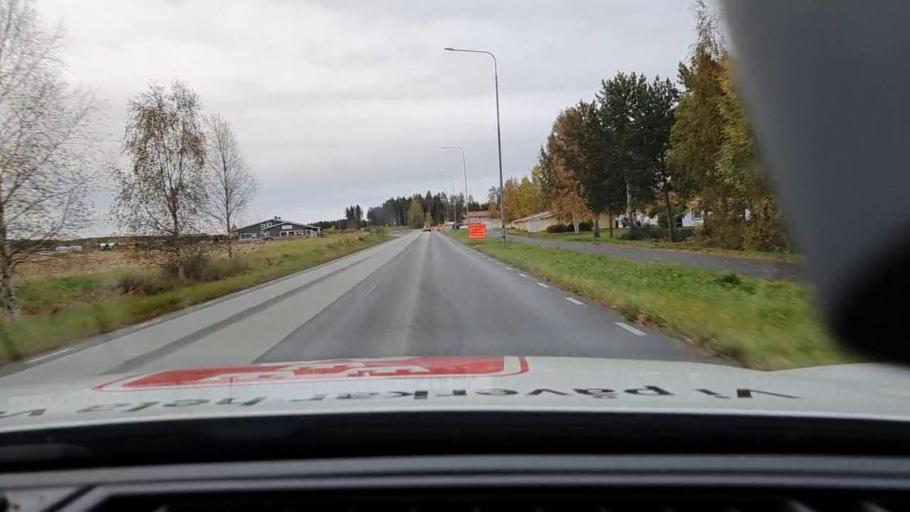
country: SE
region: Norrbotten
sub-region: Bodens Kommun
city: Saevast
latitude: 65.7562
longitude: 21.7567
